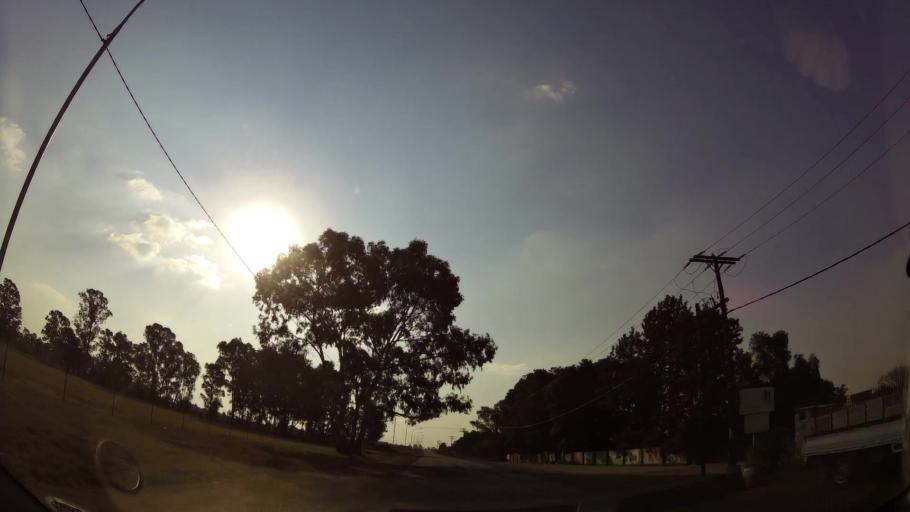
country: ZA
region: Gauteng
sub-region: Ekurhuleni Metropolitan Municipality
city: Benoni
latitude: -26.1079
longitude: 28.3856
